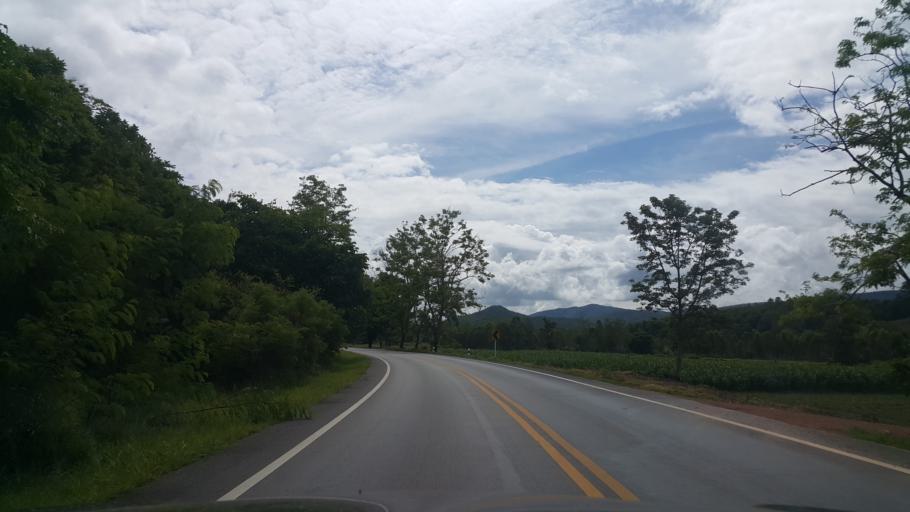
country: TH
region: Uttaradit
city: Thong Saen Khan
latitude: 17.3644
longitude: 100.2465
